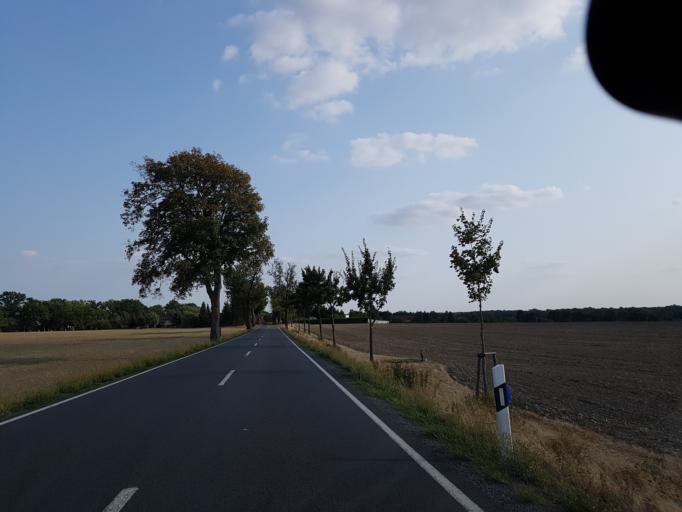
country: DE
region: Saxony
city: Elsnig
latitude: 51.6203
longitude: 12.9068
